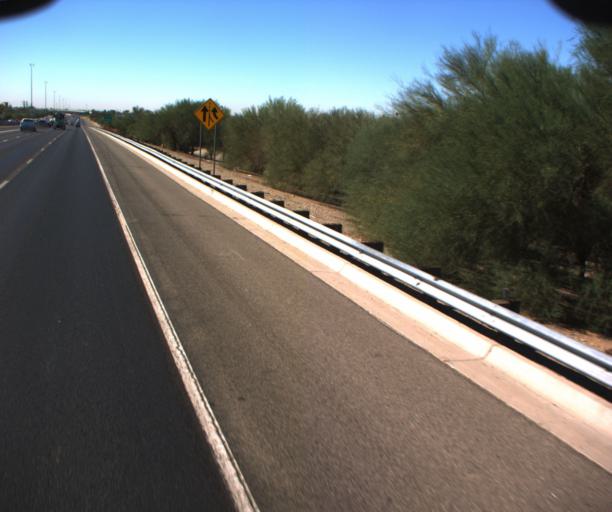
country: US
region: Arizona
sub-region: Maricopa County
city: Sun City
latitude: 33.6095
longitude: -112.2451
